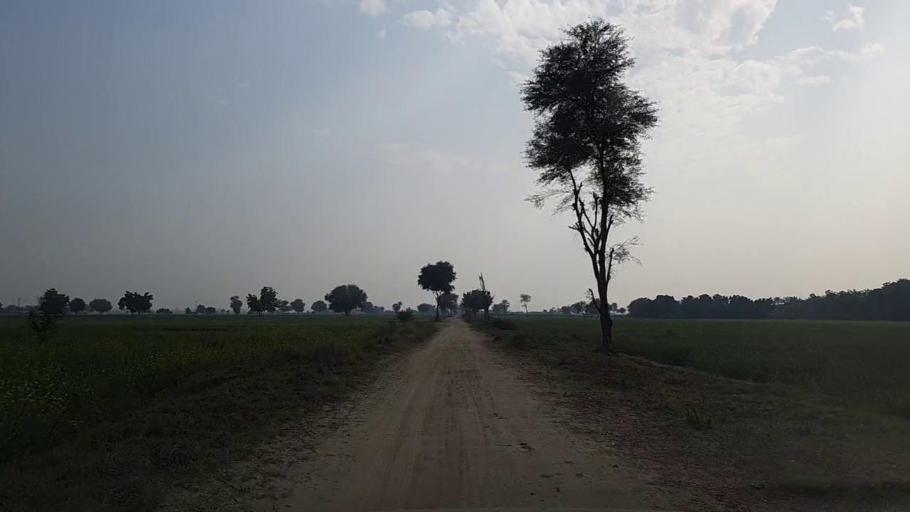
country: PK
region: Sindh
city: Nawabshah
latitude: 26.2856
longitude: 68.4457
